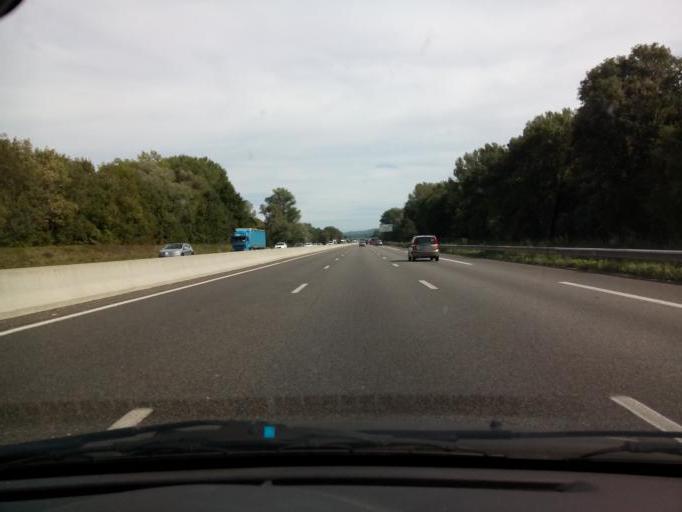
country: FR
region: Rhone-Alpes
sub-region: Departement de l'Isere
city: La Verpilliere
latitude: 45.6398
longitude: 5.1489
